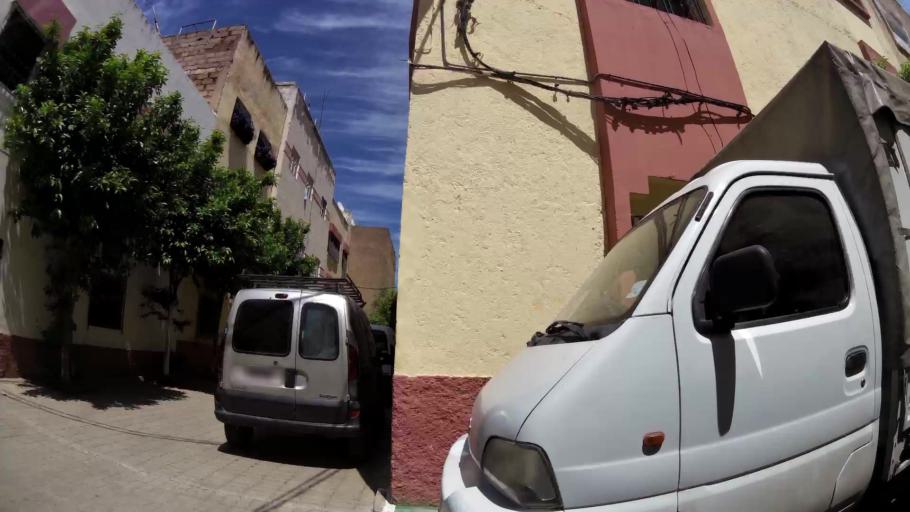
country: MA
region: Fes-Boulemane
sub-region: Fes
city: Fes
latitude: 34.0104
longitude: -4.9897
